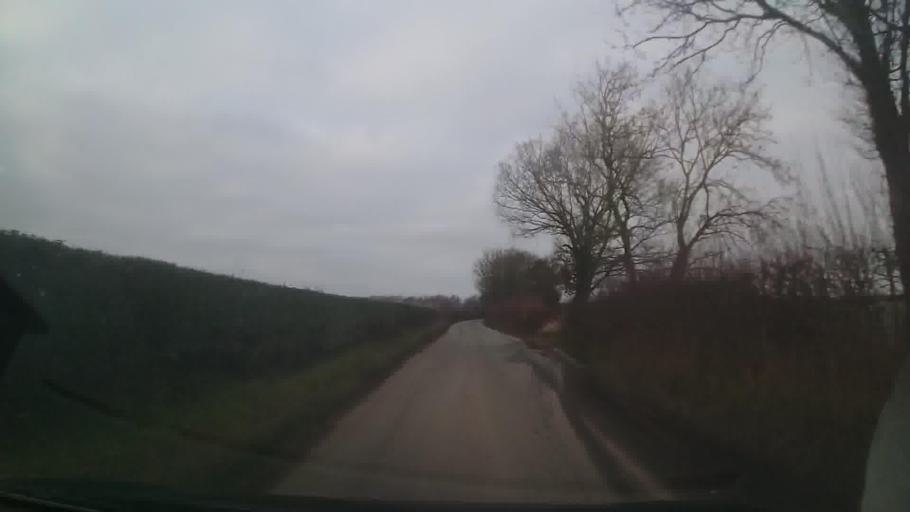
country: GB
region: England
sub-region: Shropshire
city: Great Ness
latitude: 52.7784
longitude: -2.8504
